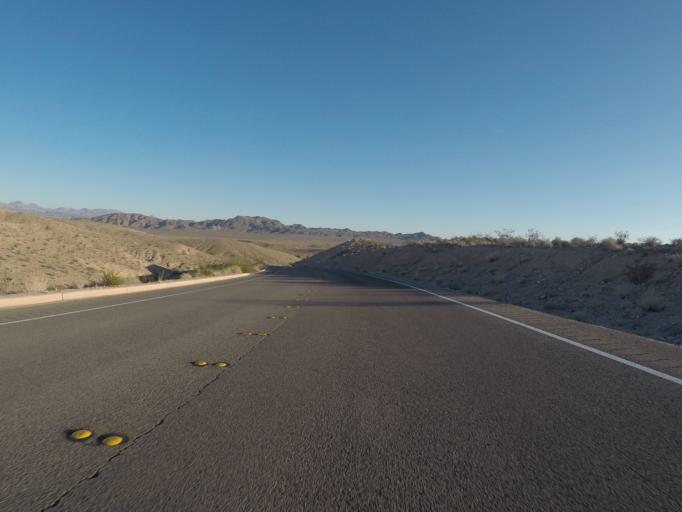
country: US
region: Nevada
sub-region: Clark County
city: Moapa Valley
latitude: 36.3136
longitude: -114.4919
